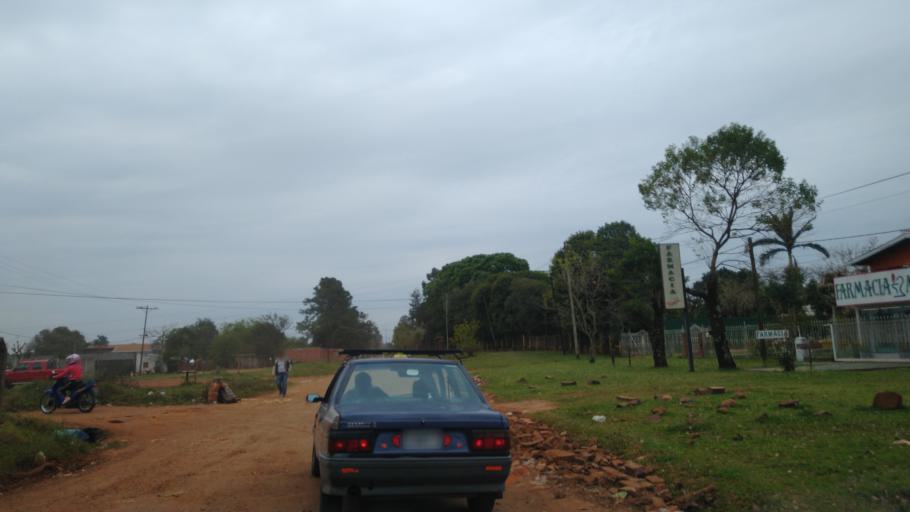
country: AR
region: Misiones
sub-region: Departamento de Capital
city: Posadas
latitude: -27.4255
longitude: -55.8950
